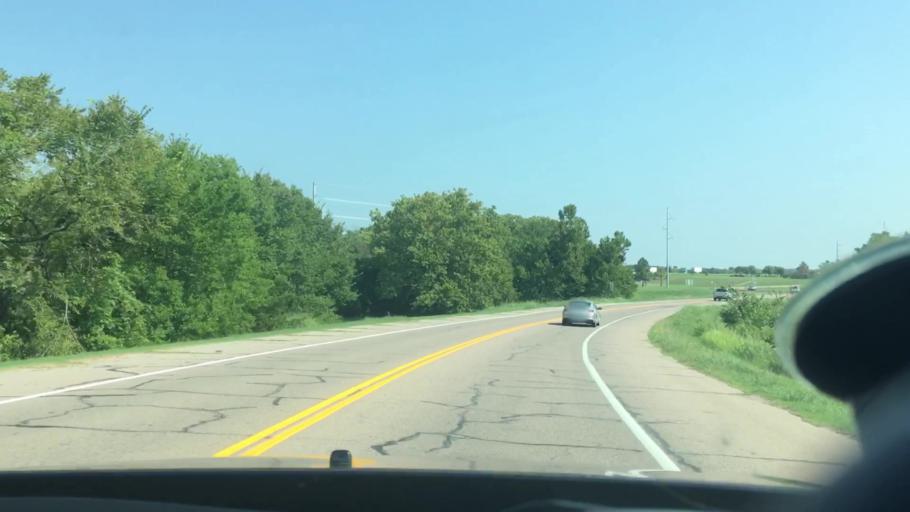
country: US
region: Oklahoma
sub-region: Bryan County
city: Durant
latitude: 34.0154
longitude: -96.3904
